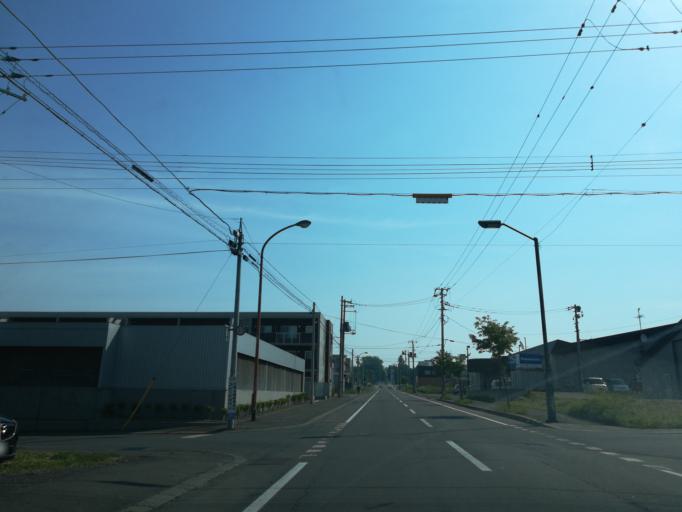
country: JP
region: Hokkaido
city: Iwamizawa
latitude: 43.2124
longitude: 141.7800
